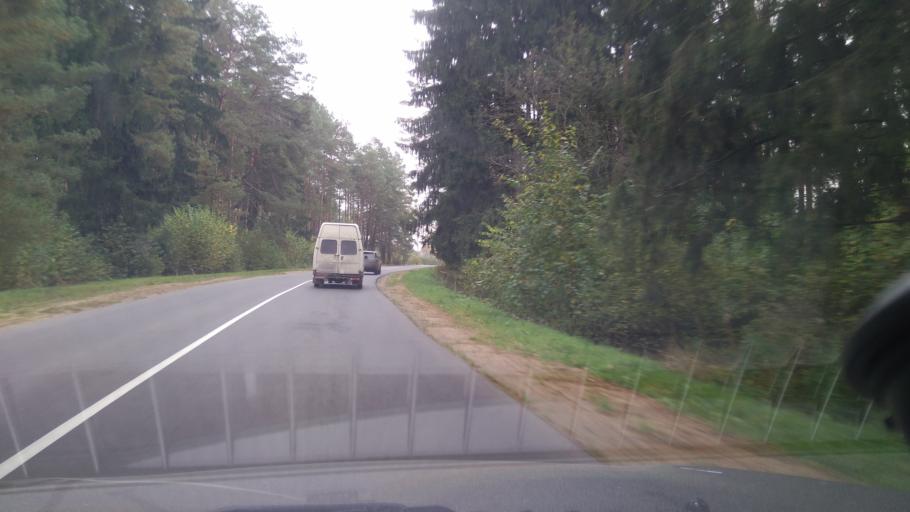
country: BY
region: Minsk
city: Rudzyensk
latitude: 53.6130
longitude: 27.7906
